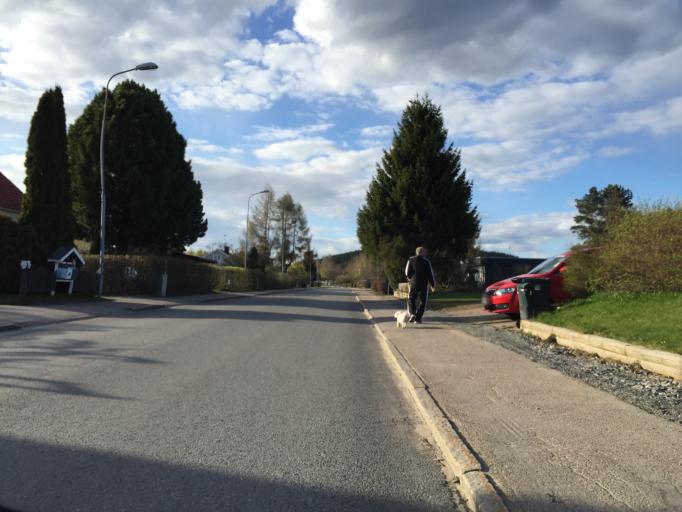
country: SE
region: Dalarna
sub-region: Ludvika Kommun
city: Ludvika
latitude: 60.1220
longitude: 15.1926
